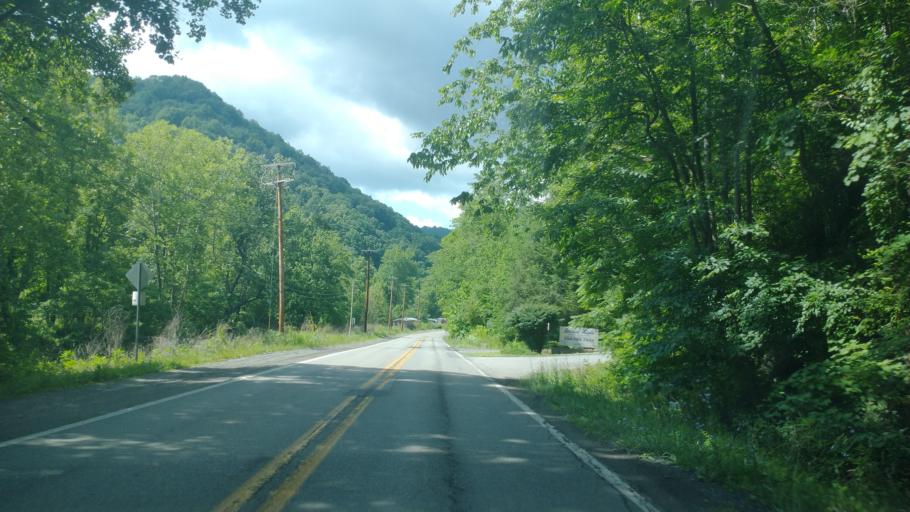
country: US
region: West Virginia
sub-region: McDowell County
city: Welch
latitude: 37.4196
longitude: -81.5183
